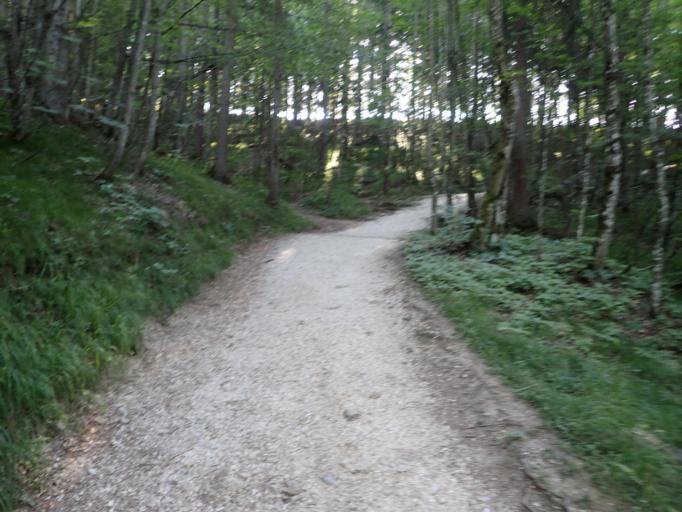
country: DE
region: Bavaria
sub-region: Upper Bavaria
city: Berchtesgaden
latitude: 47.6537
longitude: 13.0118
